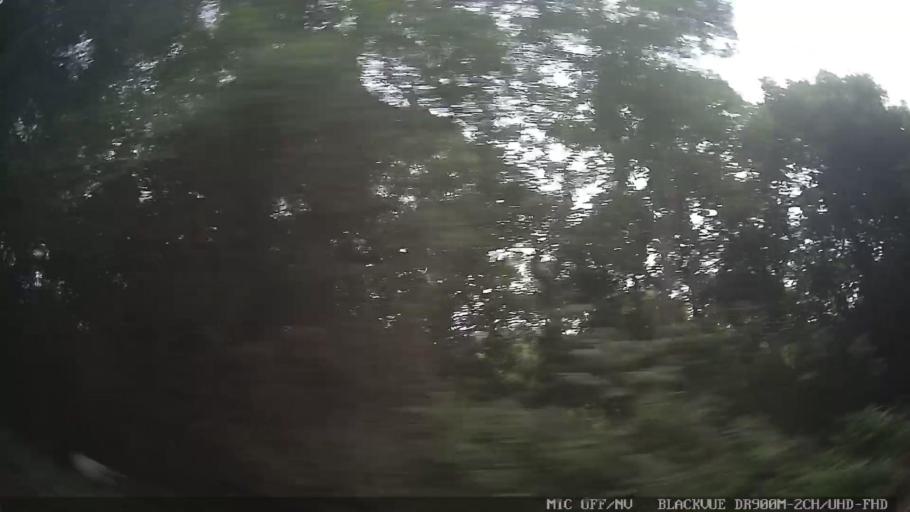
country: BR
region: Sao Paulo
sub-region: Rio Grande Da Serra
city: Rio Grande da Serra
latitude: -23.6985
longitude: -46.2704
